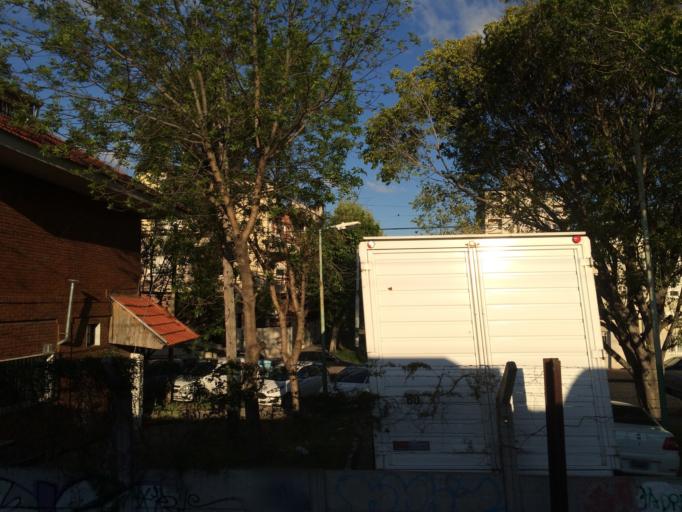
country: AR
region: Buenos Aires
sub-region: Partido de Lomas de Zamora
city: Lomas de Zamora
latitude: -34.7469
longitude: -58.3956
